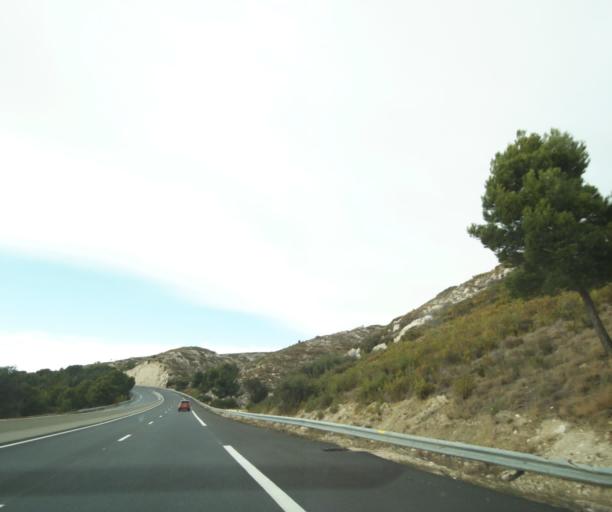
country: FR
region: Provence-Alpes-Cote d'Azur
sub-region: Departement des Bouches-du-Rhone
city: Carry-le-Rouet
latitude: 43.3425
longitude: 5.1298
